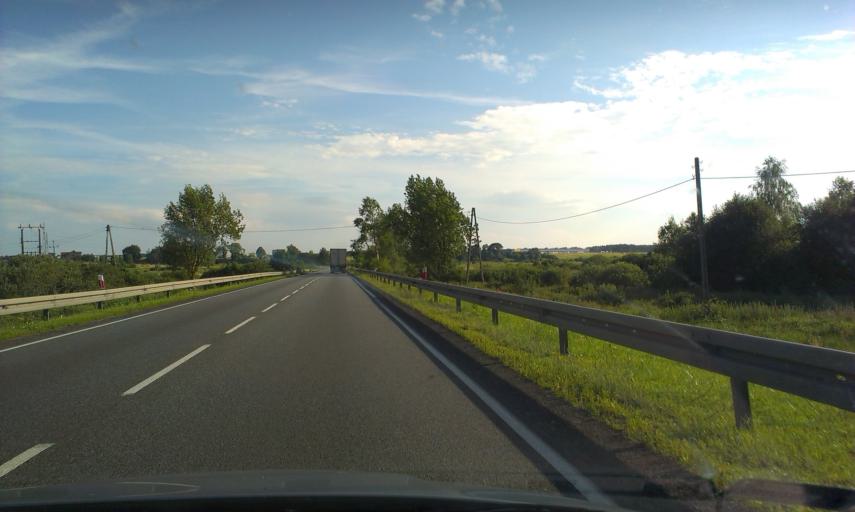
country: PL
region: Kujawsko-Pomorskie
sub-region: Powiat bydgoski
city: Biale Blota
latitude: 53.1437
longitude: 17.8811
